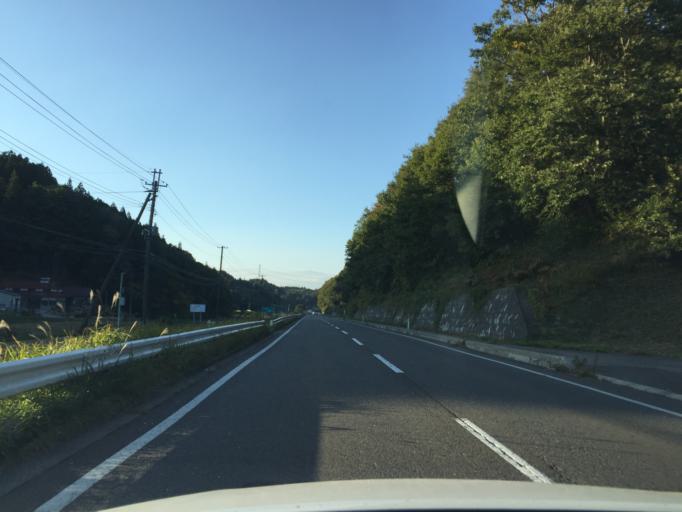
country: JP
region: Fukushima
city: Ishikawa
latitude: 37.1834
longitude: 140.6475
